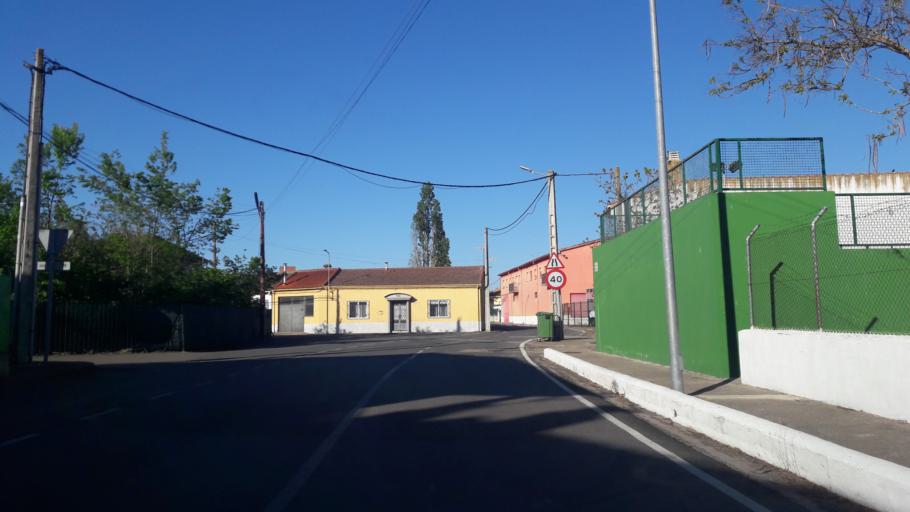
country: ES
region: Castille and Leon
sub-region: Provincia de Salamanca
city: La Fuente de San Esteban
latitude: 40.8042
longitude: -6.2578
